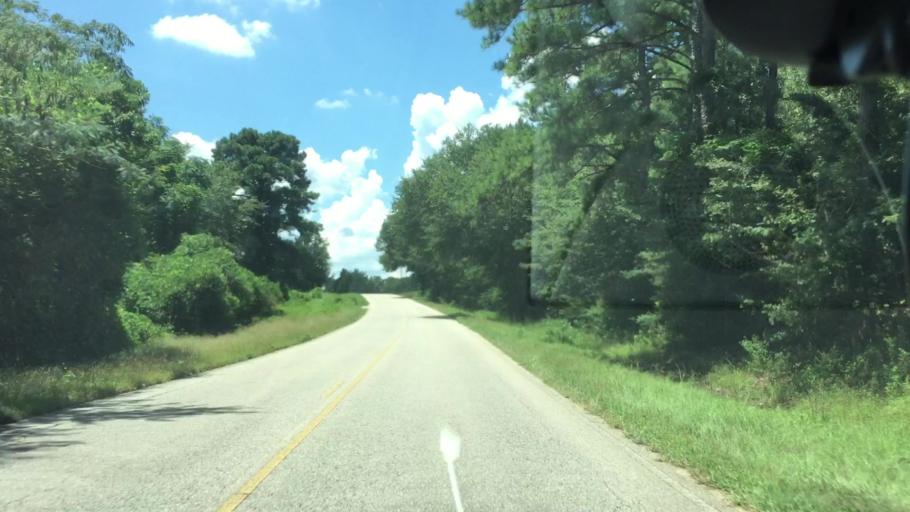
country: US
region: Alabama
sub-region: Pike County
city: Troy
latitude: 31.7467
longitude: -85.9673
